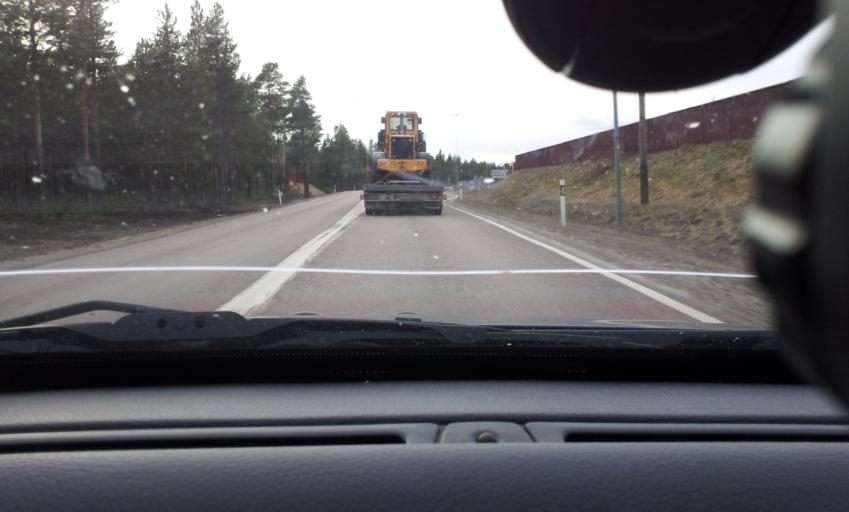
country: SE
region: Gaevleborg
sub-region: Ljusdals Kommun
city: Farila
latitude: 61.8028
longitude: 15.7884
